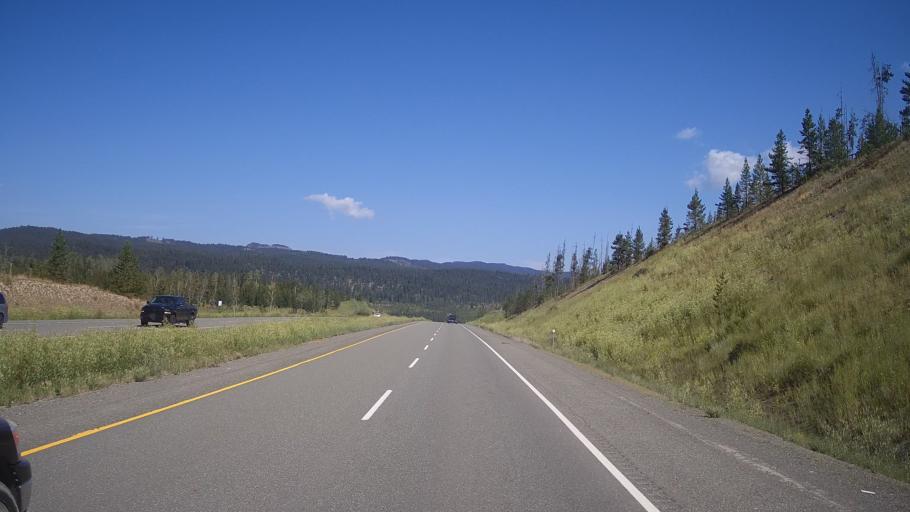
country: CA
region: British Columbia
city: Logan Lake
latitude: 50.4506
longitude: -120.5915
